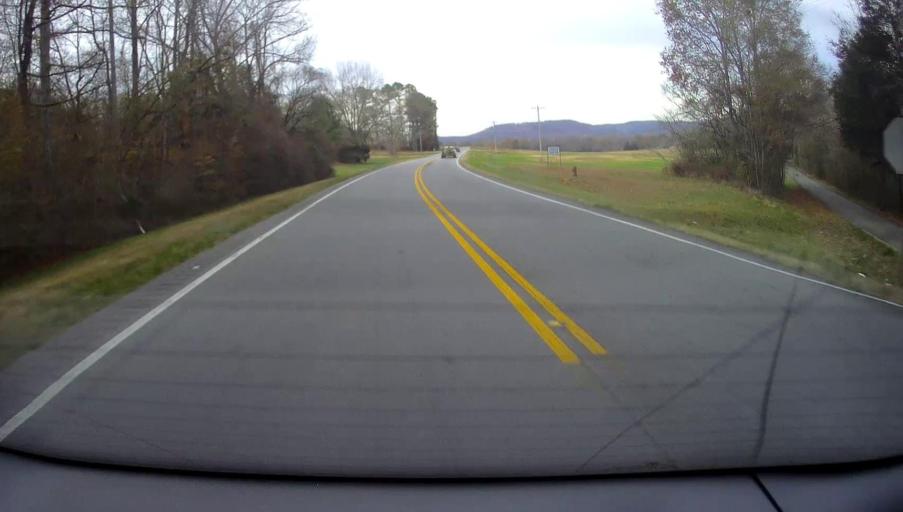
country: US
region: Alabama
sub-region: Marshall County
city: Arab
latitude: 34.3765
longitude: -86.6548
